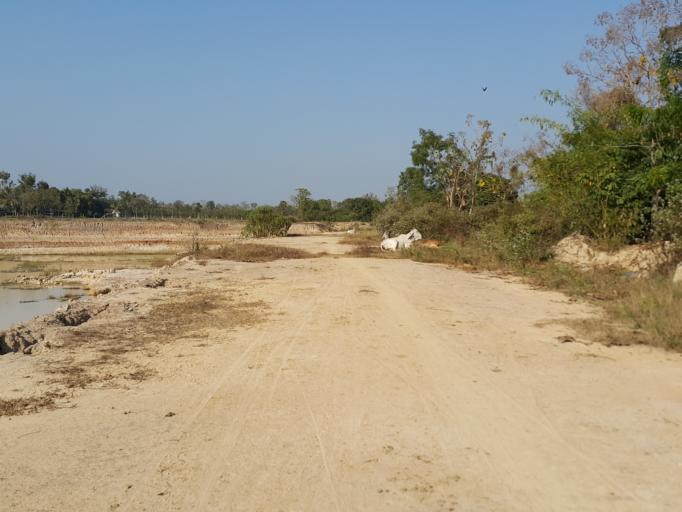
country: TH
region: Chiang Mai
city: San Kamphaeng
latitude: 18.7980
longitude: 99.0928
